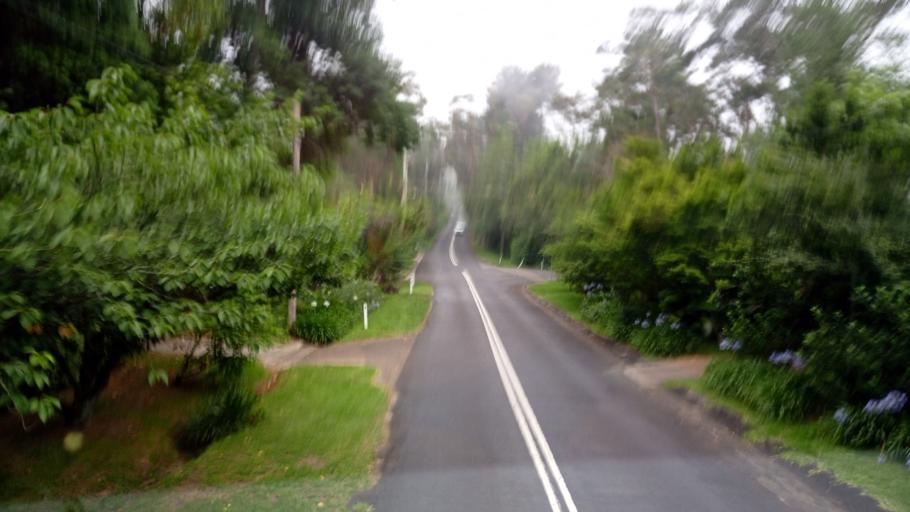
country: AU
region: New South Wales
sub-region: Blue Mountains Municipality
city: Leura
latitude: -33.7191
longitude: 150.3390
